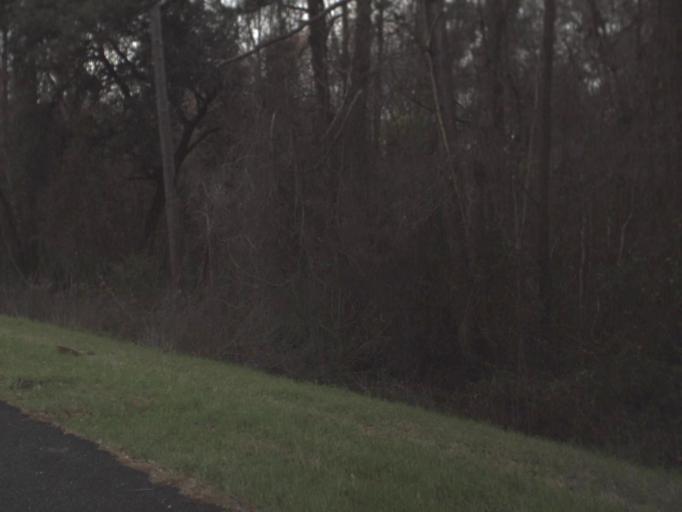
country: US
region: Florida
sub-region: Jefferson County
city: Monticello
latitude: 30.3745
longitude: -83.8106
